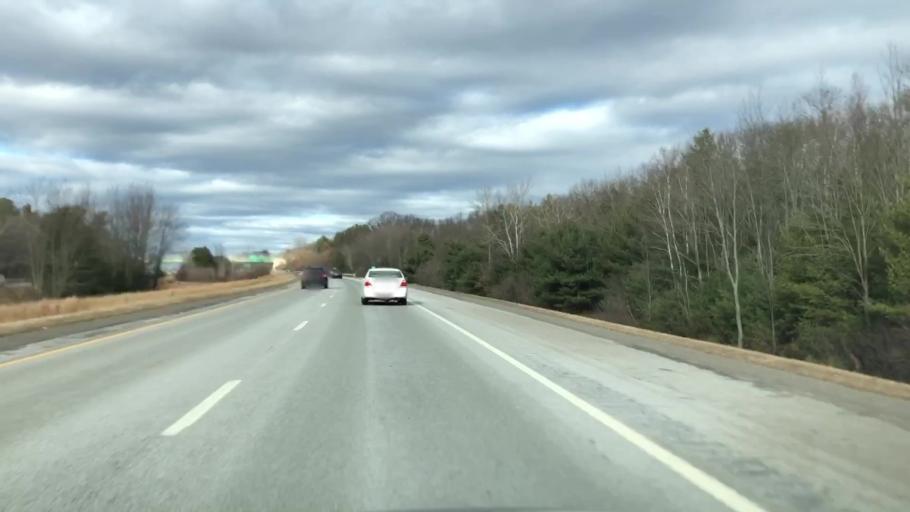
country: US
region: Massachusetts
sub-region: Worcester County
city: Leominster
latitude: 42.5033
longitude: -71.7204
